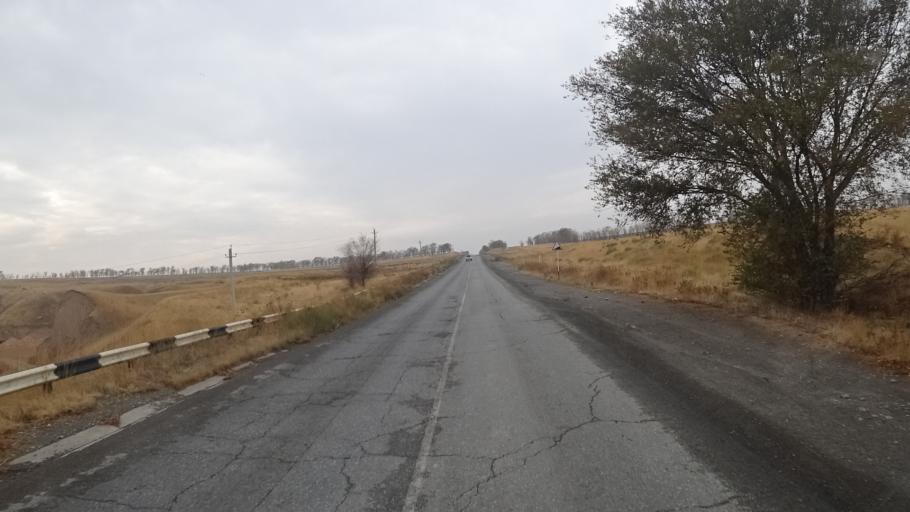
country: KZ
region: Ongtustik Qazaqstan
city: Aksu
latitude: 42.4209
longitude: 69.6947
